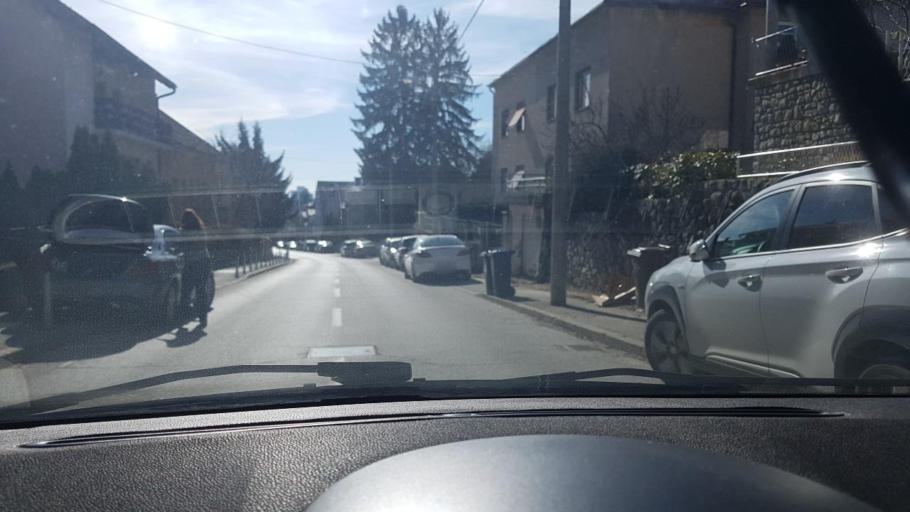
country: HR
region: Grad Zagreb
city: Zagreb - Centar
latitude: 45.8194
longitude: 15.9525
